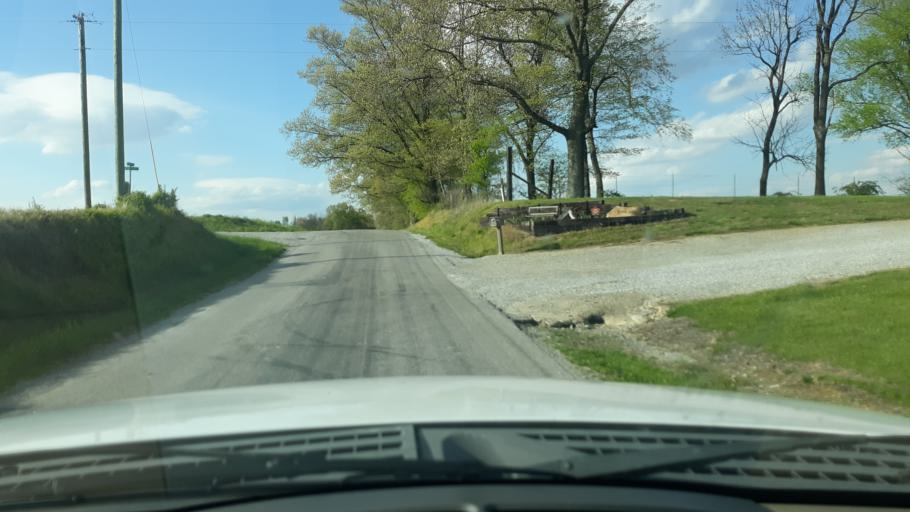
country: US
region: Illinois
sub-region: Saline County
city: Harrisburg
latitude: 37.8118
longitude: -88.6146
